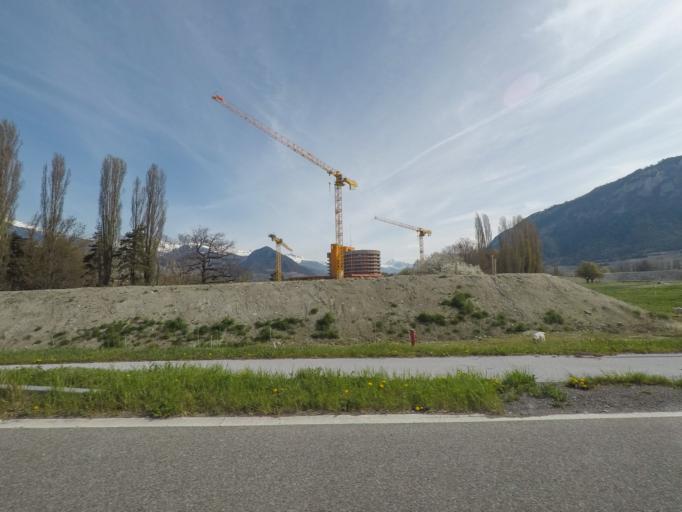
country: CH
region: Valais
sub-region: Sion District
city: Sitten
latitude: 46.2330
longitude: 7.3837
